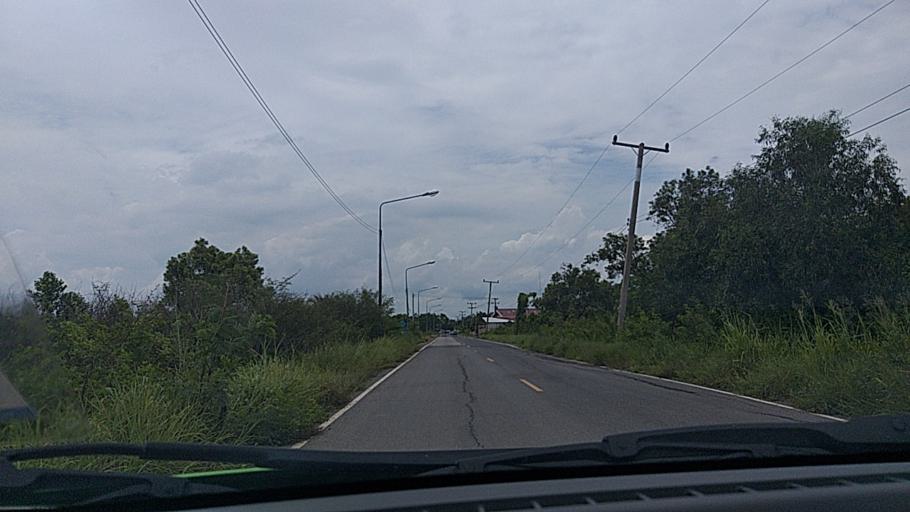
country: TH
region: Nakhon Nayok
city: Ongkharak
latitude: 14.0922
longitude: 100.9549
